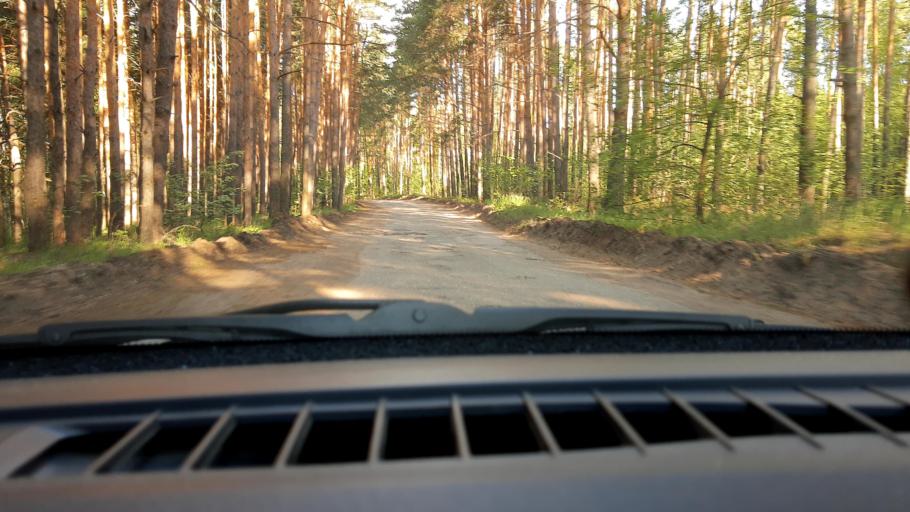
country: RU
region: Nizjnij Novgorod
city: Sitniki
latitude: 56.4160
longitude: 44.0479
